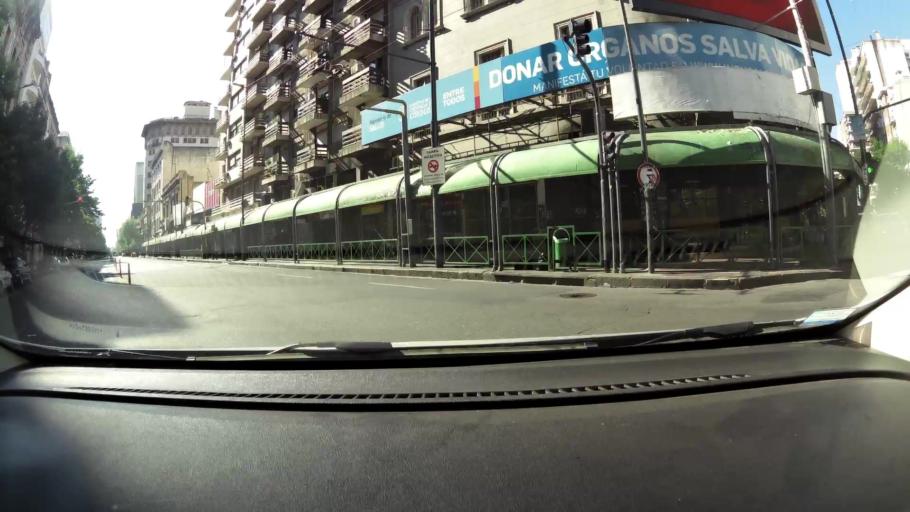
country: AR
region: Cordoba
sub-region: Departamento de Capital
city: Cordoba
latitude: -31.4129
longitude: -64.1858
